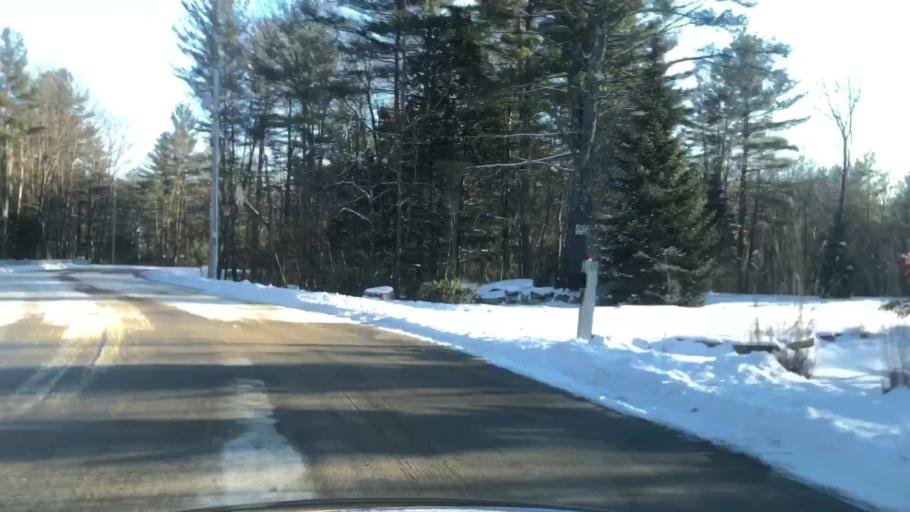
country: US
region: New Hampshire
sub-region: Hillsborough County
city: Milford
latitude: 42.7975
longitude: -71.6652
